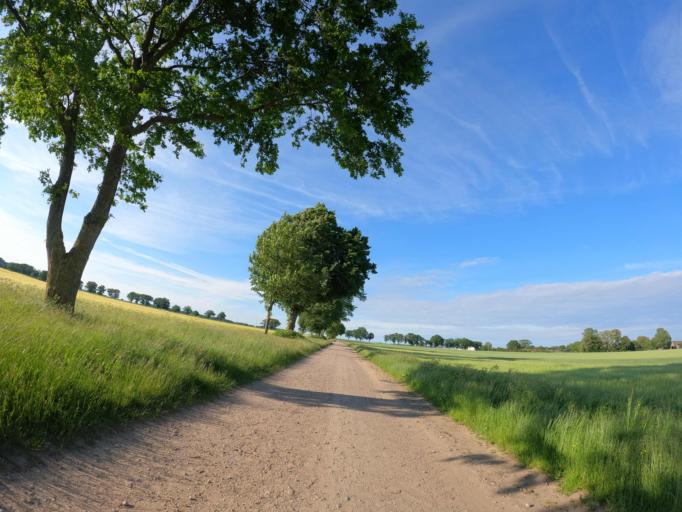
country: DE
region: Mecklenburg-Vorpommern
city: Preetz
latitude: 54.3449
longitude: 12.9999
